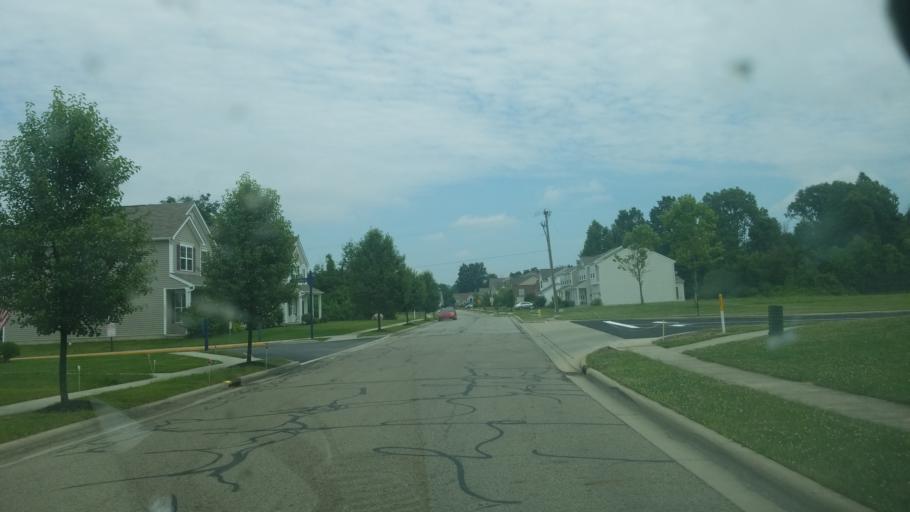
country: US
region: Ohio
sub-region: Franklin County
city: Reynoldsburg
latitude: 40.0133
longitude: -82.7829
